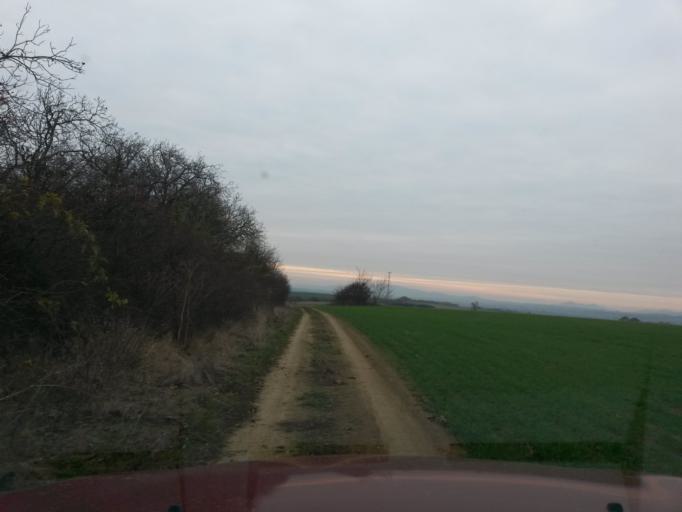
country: SK
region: Kosicky
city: Secovce
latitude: 48.6472
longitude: 21.6229
